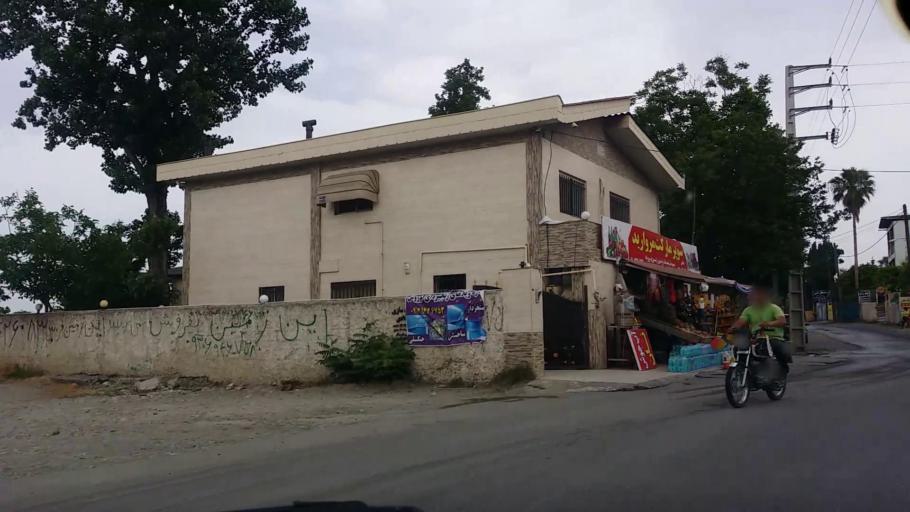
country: IR
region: Mazandaran
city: Chalus
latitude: 36.6863
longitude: 51.4057
